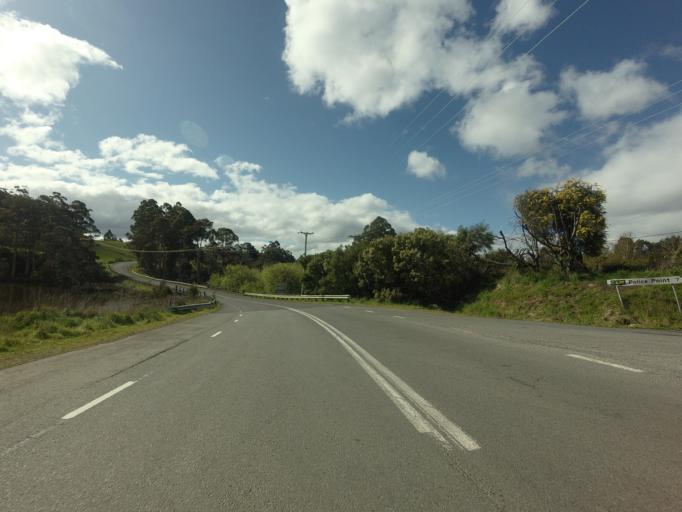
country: AU
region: Tasmania
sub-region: Huon Valley
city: Geeveston
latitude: -43.2178
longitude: 146.9899
